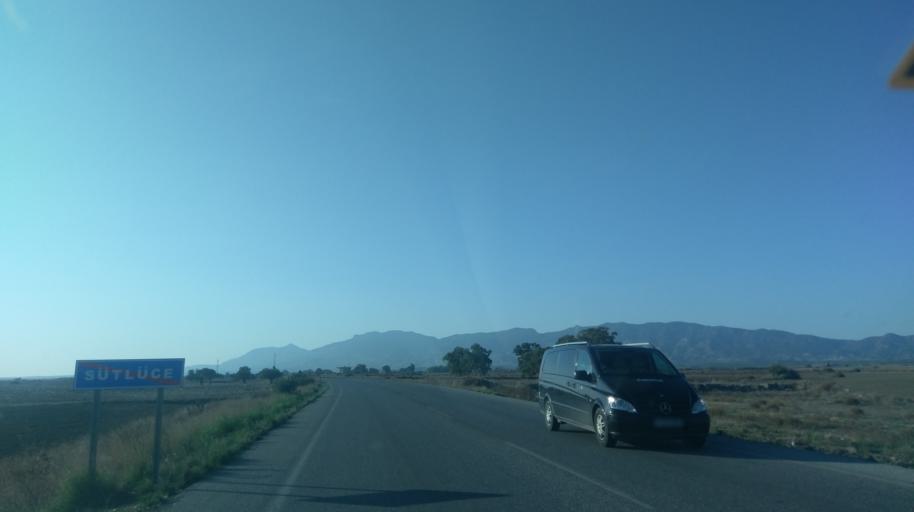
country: CY
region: Ammochostos
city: Lefkonoiko
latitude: 35.2576
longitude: 33.6806
